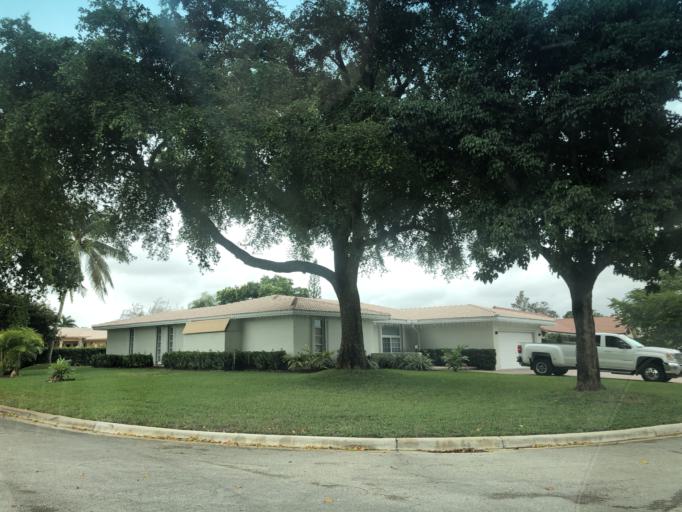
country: US
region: Florida
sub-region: Broward County
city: North Lauderdale
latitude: 26.2419
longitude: -80.2372
